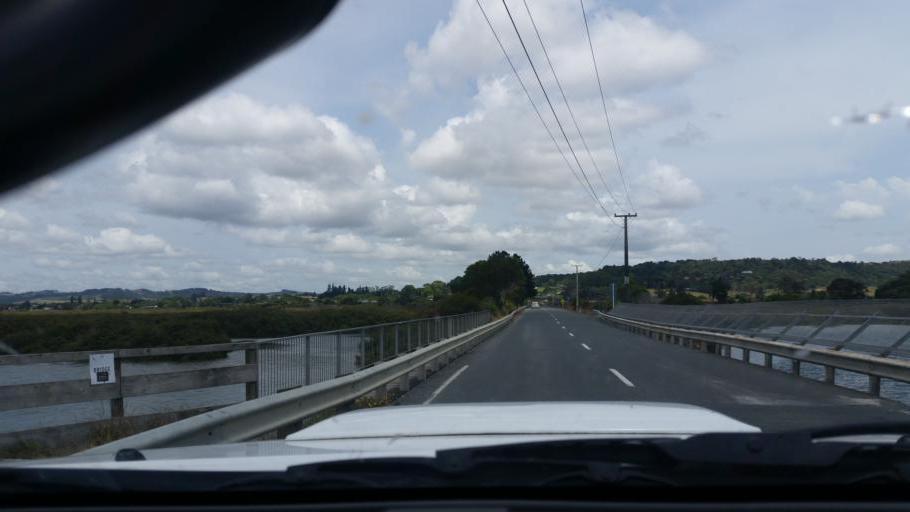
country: NZ
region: Auckland
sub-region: Auckland
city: Wellsford
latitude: -36.1085
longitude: 174.5796
